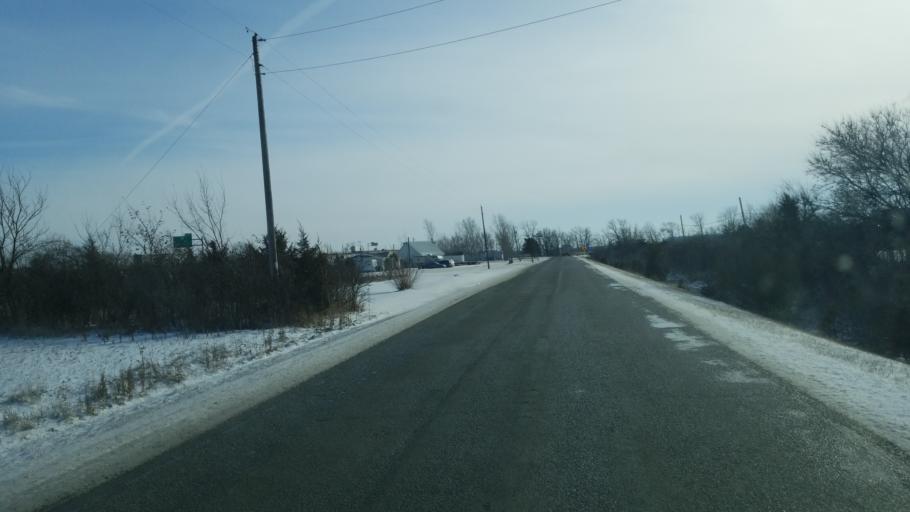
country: US
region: Ohio
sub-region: Wood County
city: North Baltimore
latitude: 41.1850
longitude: -83.6512
